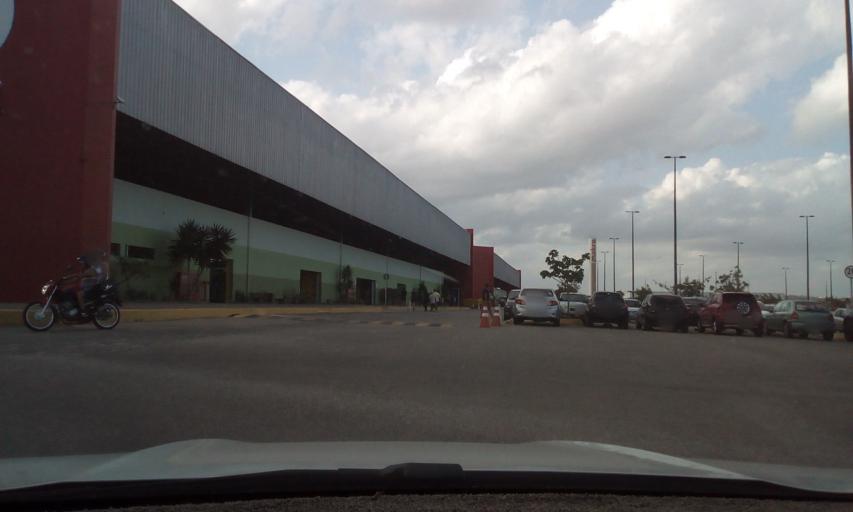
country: BR
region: Pernambuco
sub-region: Caruaru
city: Caruaru
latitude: -8.2408
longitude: -35.9794
